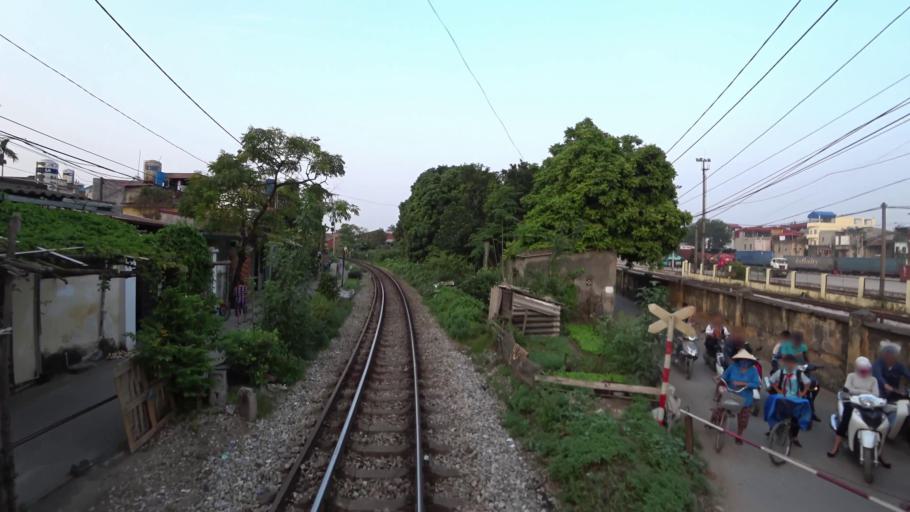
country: VN
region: Ha Noi
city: Dong Anh
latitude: 21.1075
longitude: 105.8994
